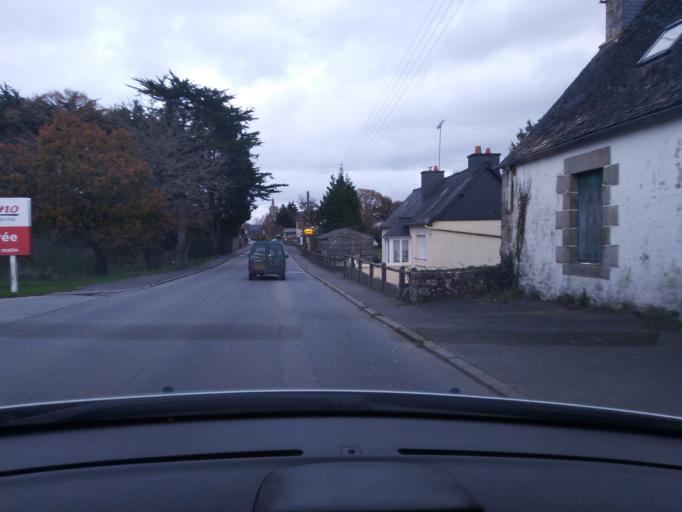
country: FR
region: Brittany
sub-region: Departement des Cotes-d'Armor
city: Plouaret
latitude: 48.6087
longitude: -3.4775
